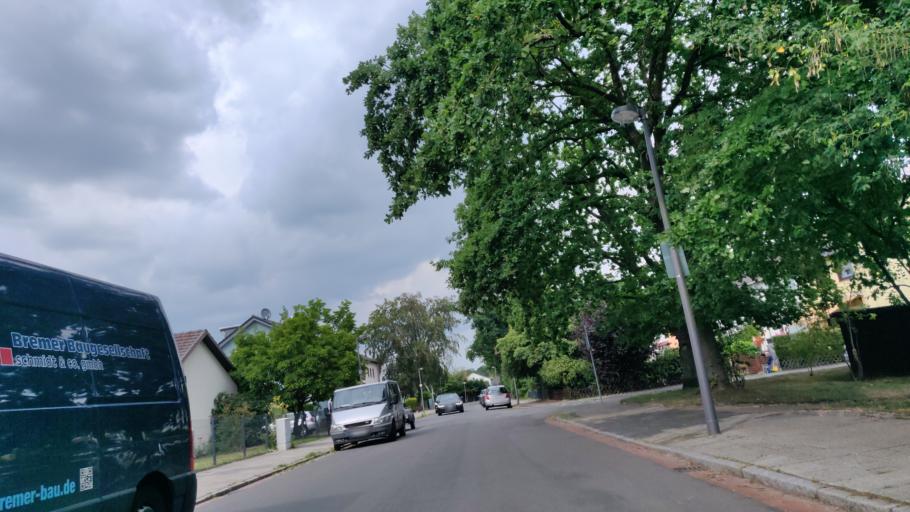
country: DE
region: Lower Saxony
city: Lilienthal
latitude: 53.1034
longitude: 8.8857
